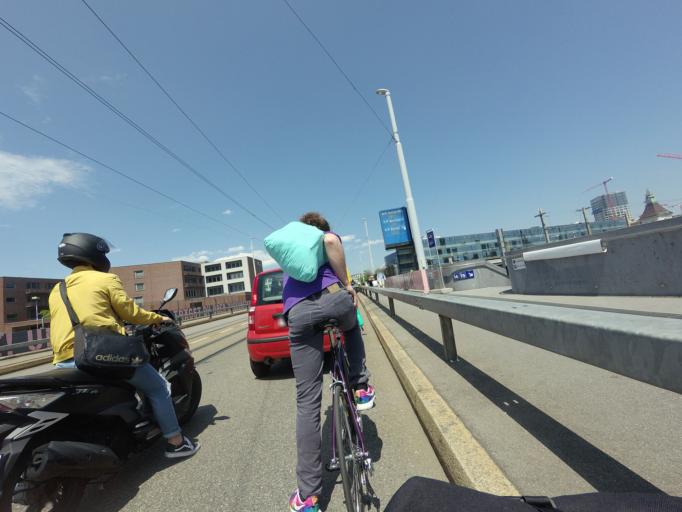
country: CH
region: Basel-City
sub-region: Basel-Stadt
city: Basel
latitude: 47.5476
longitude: 7.5850
